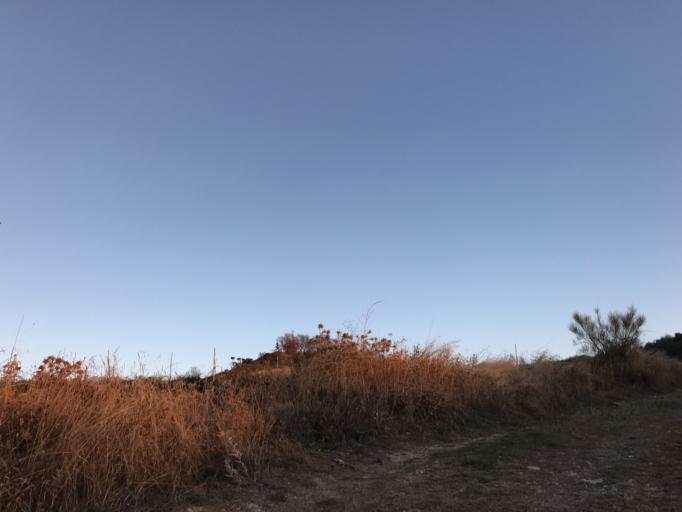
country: ES
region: Andalusia
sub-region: Provincia de Granada
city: Beas de Granada
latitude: 37.2218
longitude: -3.4693
